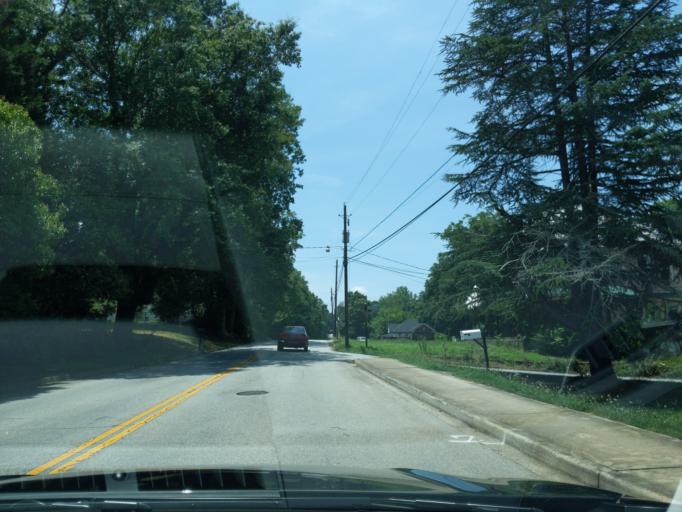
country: US
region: South Carolina
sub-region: Laurens County
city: Laurens
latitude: 34.4947
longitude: -82.0189
